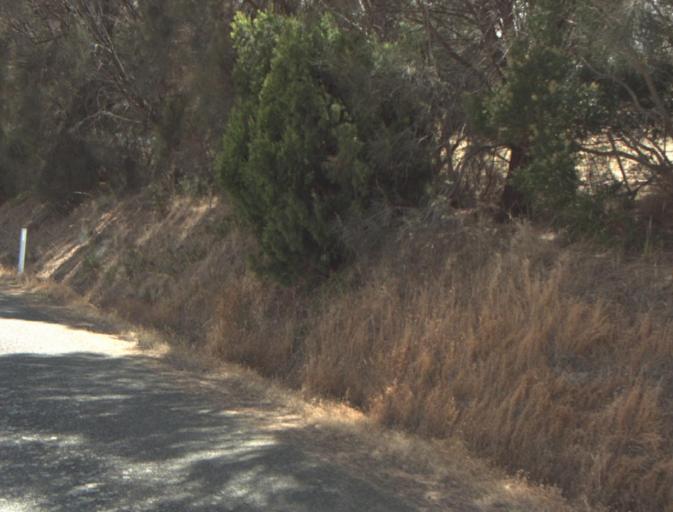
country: AU
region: Tasmania
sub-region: Northern Midlands
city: Evandale
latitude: -41.5119
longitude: 147.2900
